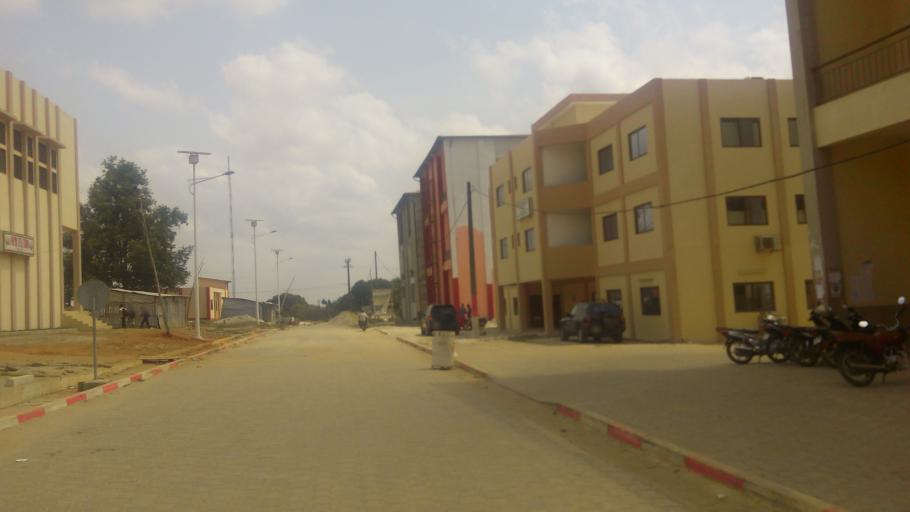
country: BJ
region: Atlantique
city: Abomey-Calavi
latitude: 6.4192
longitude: 2.3456
